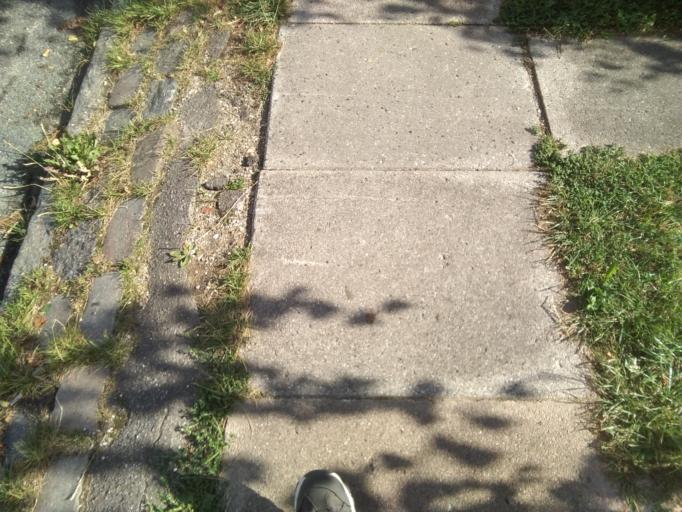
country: DK
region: Capital Region
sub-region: Kobenhavn
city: Vanlose
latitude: 55.7022
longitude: 12.4891
